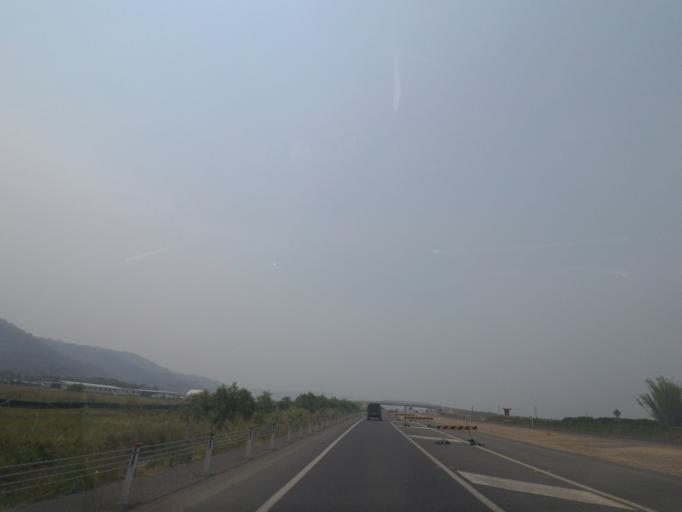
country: AU
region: New South Wales
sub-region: Ballina
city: Ballina
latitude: -28.9057
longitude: 153.4789
